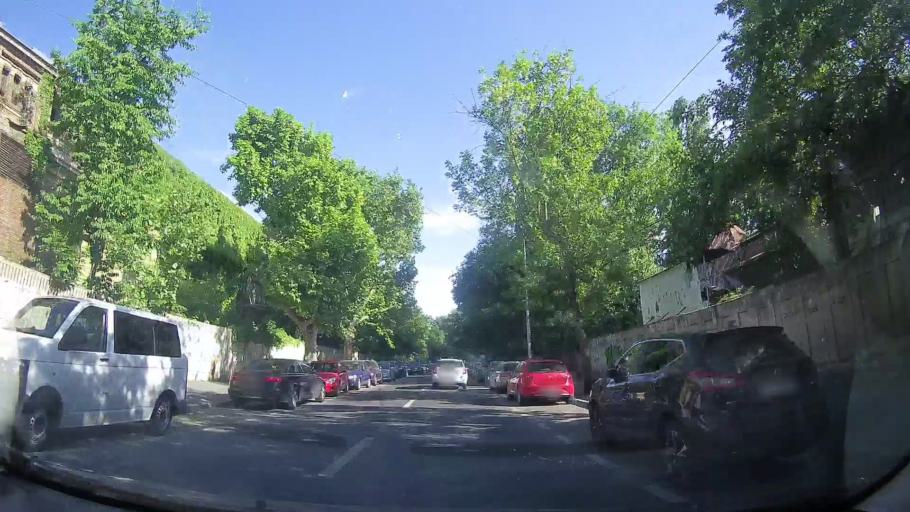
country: RO
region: Bucuresti
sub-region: Municipiul Bucuresti
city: Bucuresti
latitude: 44.4159
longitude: 26.0976
